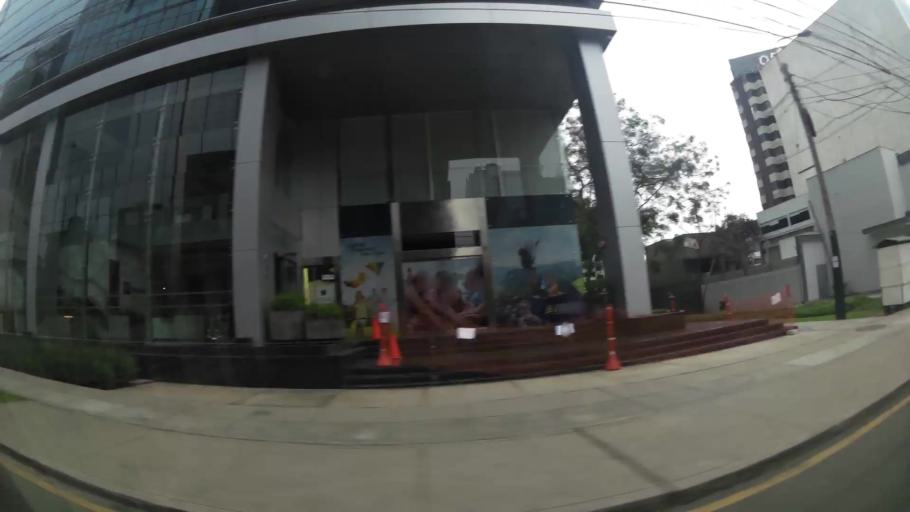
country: PE
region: Lima
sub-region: Lima
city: San Isidro
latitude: -12.0940
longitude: -77.0280
